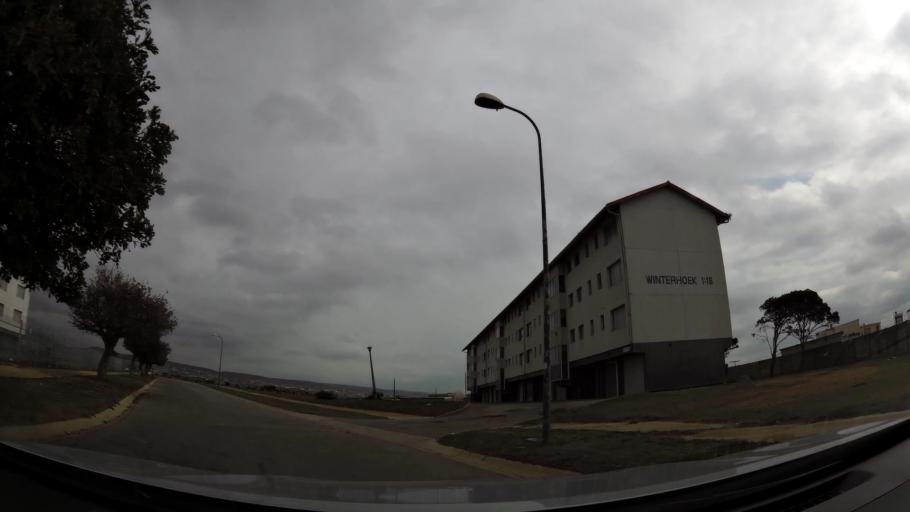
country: ZA
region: Eastern Cape
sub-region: Nelson Mandela Bay Metropolitan Municipality
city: Port Elizabeth
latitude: -33.8883
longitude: 25.5607
